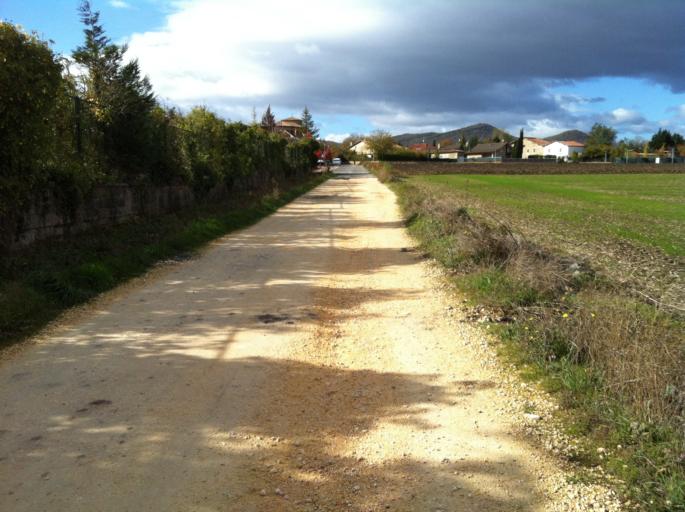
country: ES
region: Basque Country
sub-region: Provincia de Alava
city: Gasteiz / Vitoria
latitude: 42.8202
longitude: -2.6872
